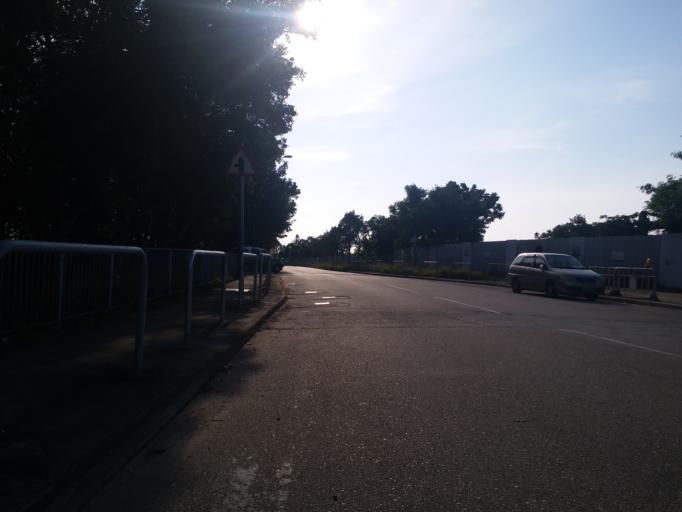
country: HK
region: Yuen Long
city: Yuen Long Kau Hui
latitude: 22.4790
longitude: 114.0570
